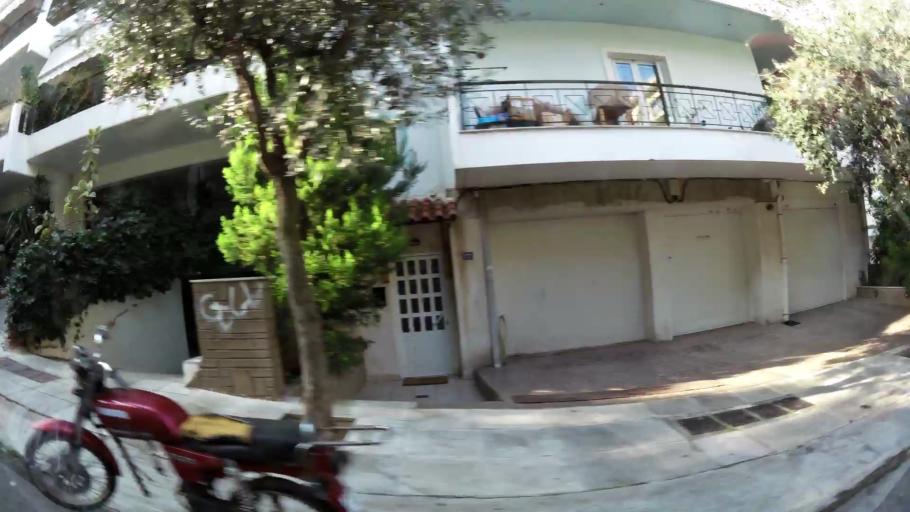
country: GR
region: Attica
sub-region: Nomarchia Athinas
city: Kaisariani
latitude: 37.9726
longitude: 23.7742
